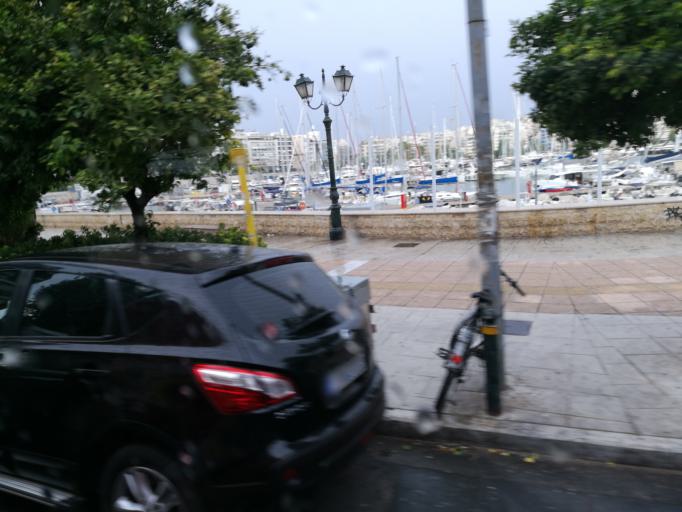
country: GR
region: Attica
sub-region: Nomos Attikis
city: Piraeus
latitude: 37.9360
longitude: 23.6459
